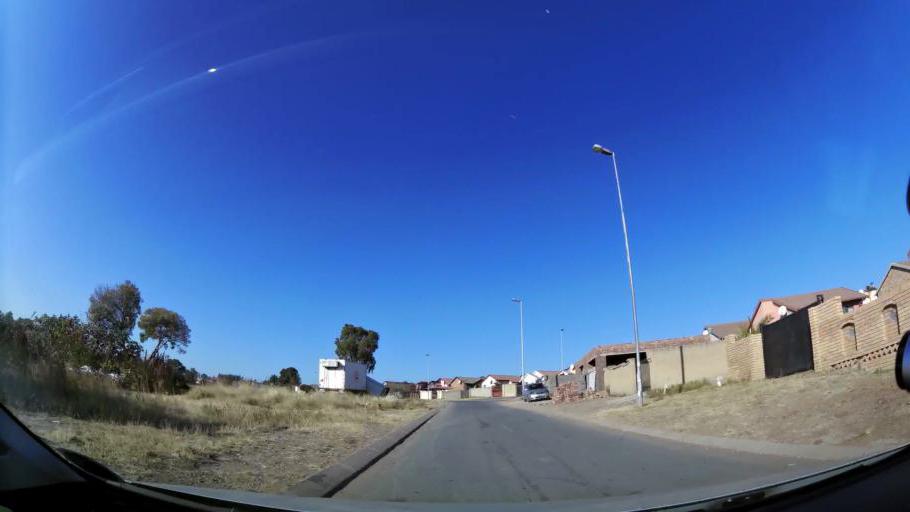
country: ZA
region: Gauteng
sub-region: City of Johannesburg Metropolitan Municipality
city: Modderfontein
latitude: -26.0434
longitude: 28.1536
